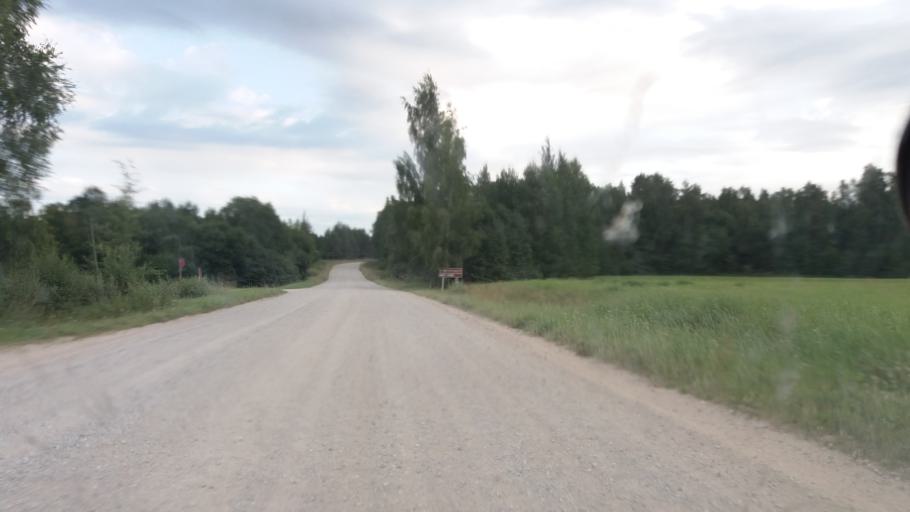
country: LV
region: Talsu Rajons
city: Sabile
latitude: 57.0228
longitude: 22.5867
